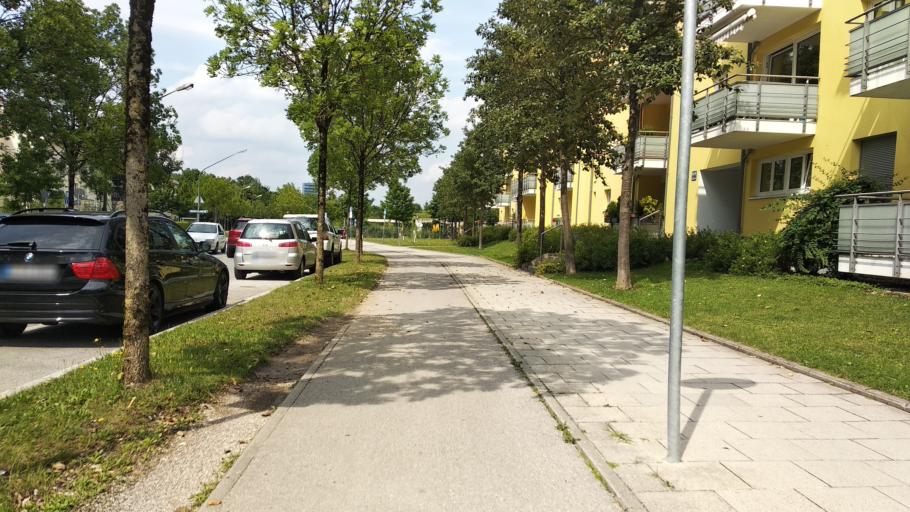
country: DE
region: Bavaria
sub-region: Upper Bavaria
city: Bogenhausen
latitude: 48.1212
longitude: 11.6318
